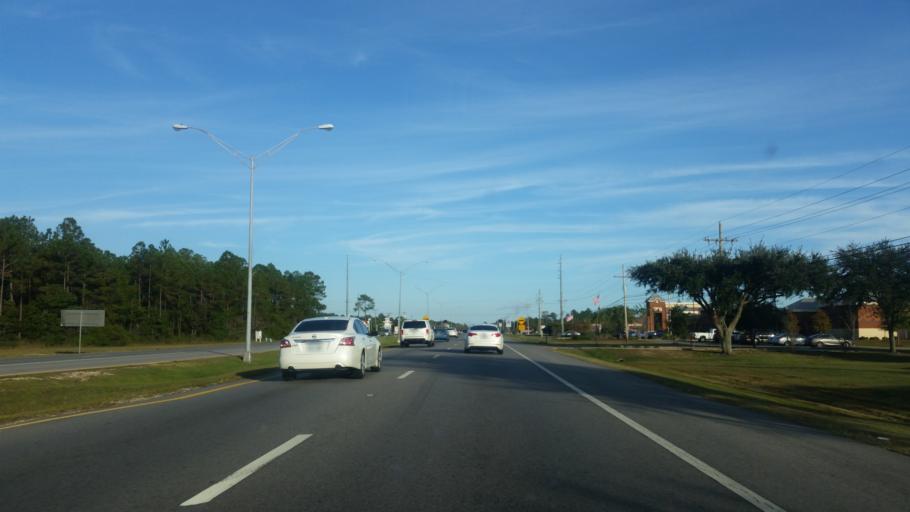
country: US
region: Mississippi
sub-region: Jackson County
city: Gulf Park Estates
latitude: 30.4100
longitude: -88.7667
